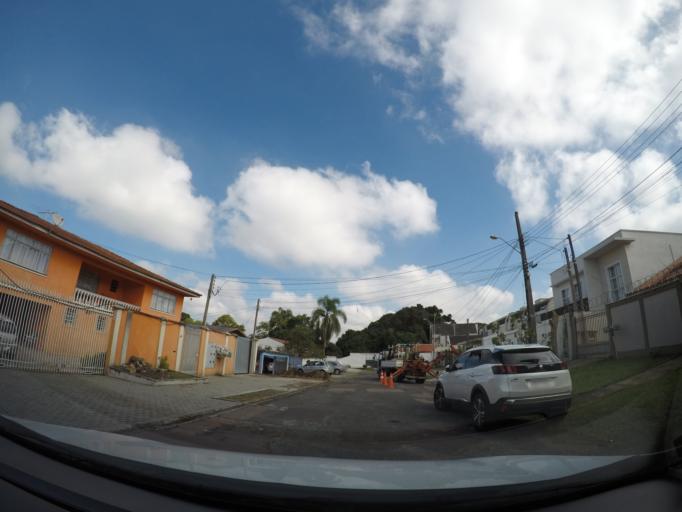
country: BR
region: Parana
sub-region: Sao Jose Dos Pinhais
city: Sao Jose dos Pinhais
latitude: -25.4933
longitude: -49.2184
